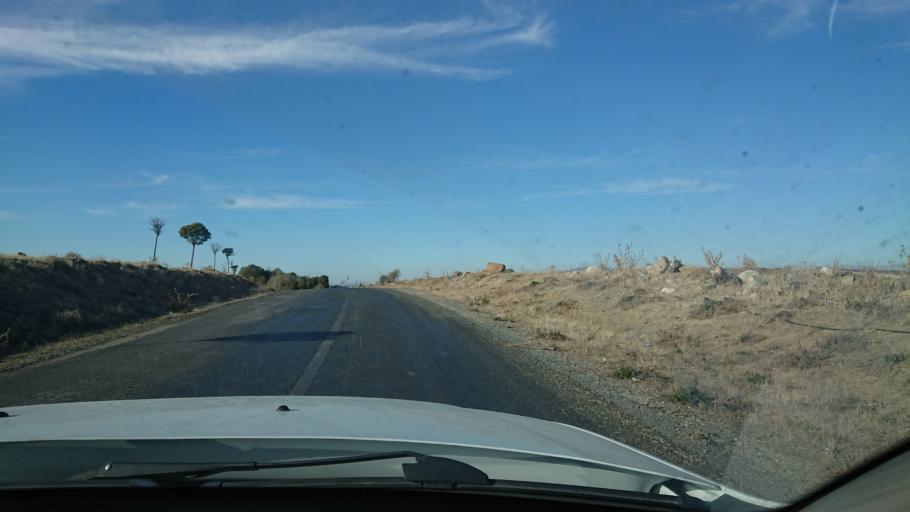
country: TR
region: Aksaray
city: Sariyahsi
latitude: 38.9689
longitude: 33.8686
